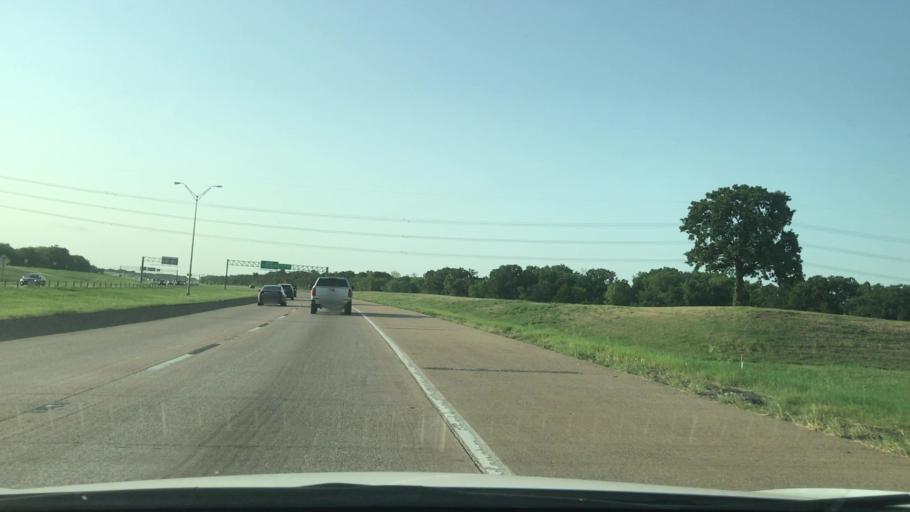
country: US
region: Texas
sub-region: Tarrant County
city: Euless
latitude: 32.8680
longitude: -97.0656
